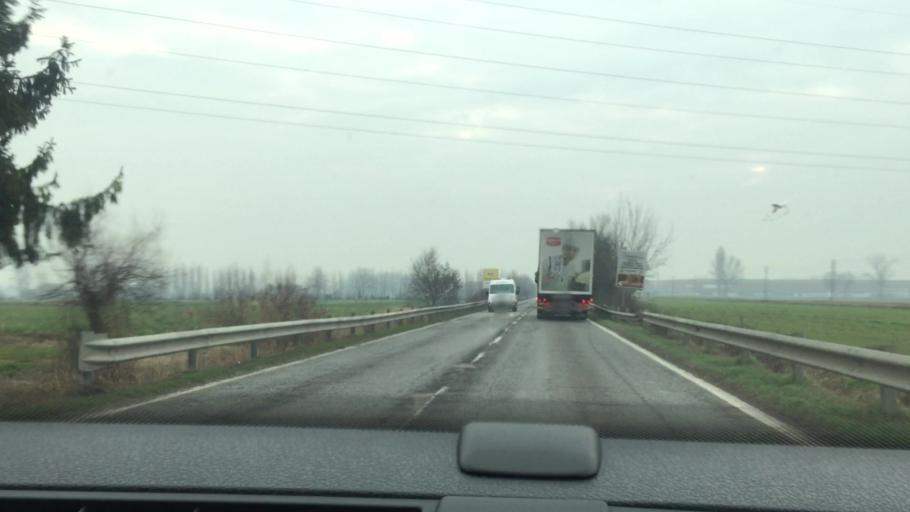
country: IT
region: Lombardy
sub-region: Provincia di Mantova
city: Cerlongo
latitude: 45.2934
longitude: 10.6249
